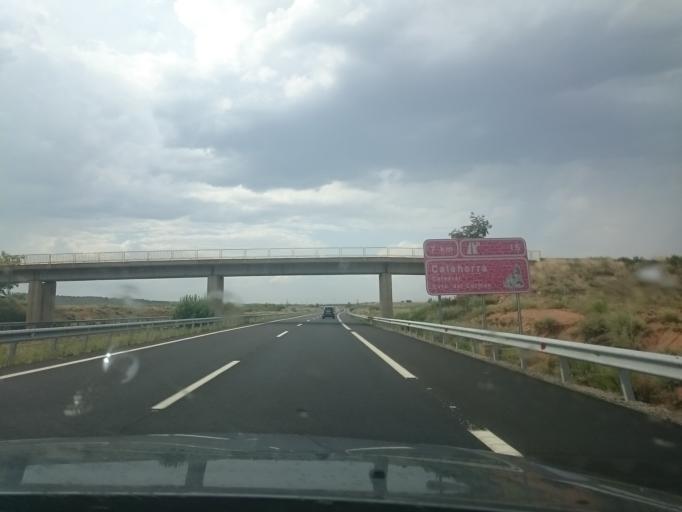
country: ES
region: Navarre
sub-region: Provincia de Navarra
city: Azagra
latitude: 42.2601
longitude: -1.9242
